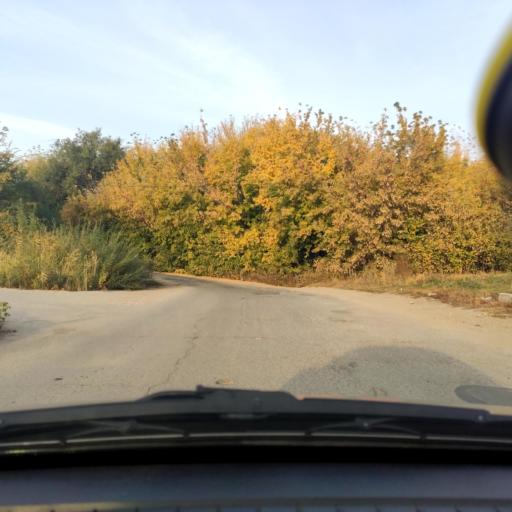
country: RU
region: Samara
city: Tol'yatti
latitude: 53.5545
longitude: 49.3207
